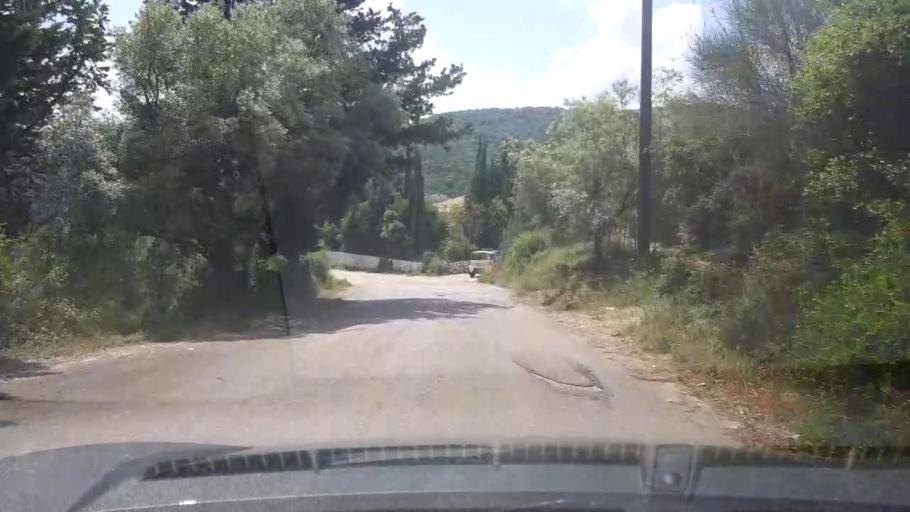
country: GR
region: Ionian Islands
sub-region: Lefkada
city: Nidri
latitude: 38.6438
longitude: 20.6973
